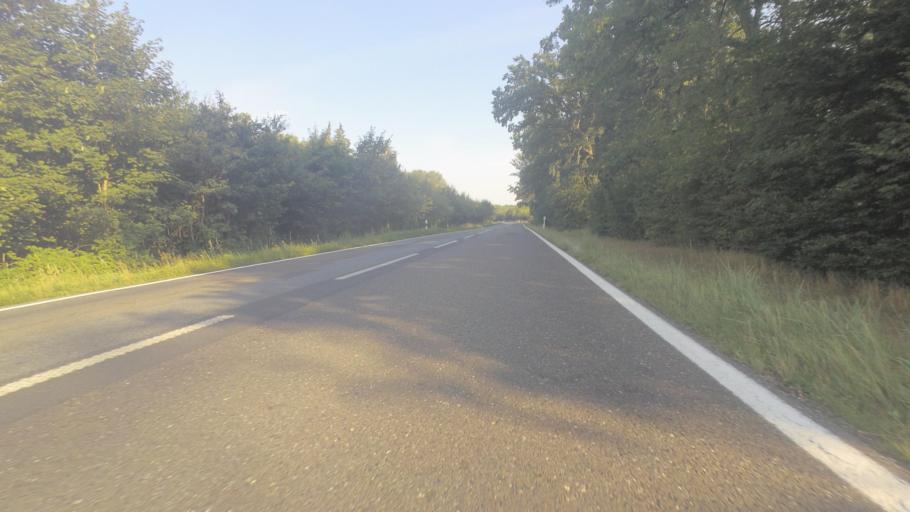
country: DE
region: Mecklenburg-Vorpommern
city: Grimmen
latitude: 54.0748
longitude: 13.1119
